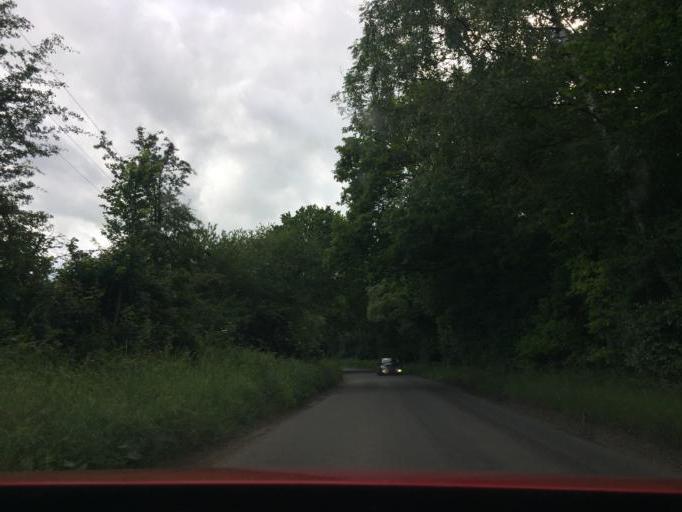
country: GB
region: England
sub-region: Hertfordshire
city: Harpenden
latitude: 51.8582
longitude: -0.3564
